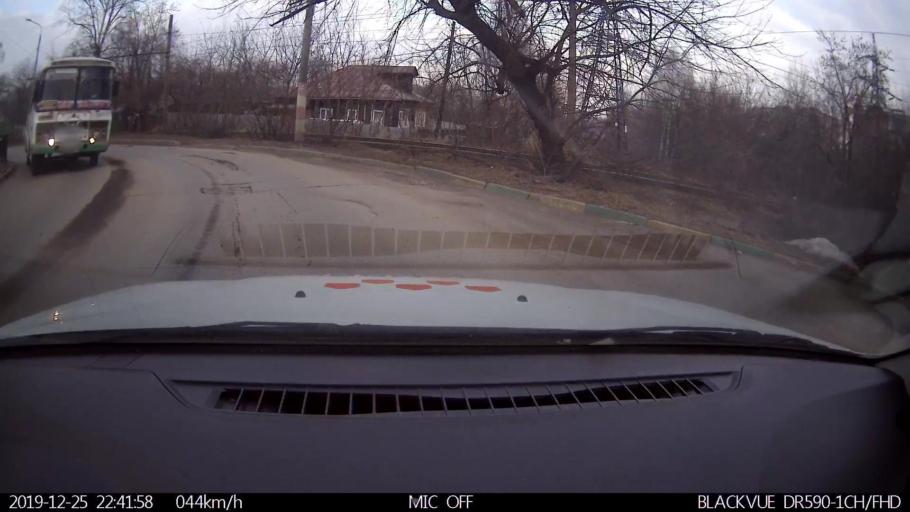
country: RU
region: Nizjnij Novgorod
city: Nizhniy Novgorod
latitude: 56.3336
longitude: 43.8689
